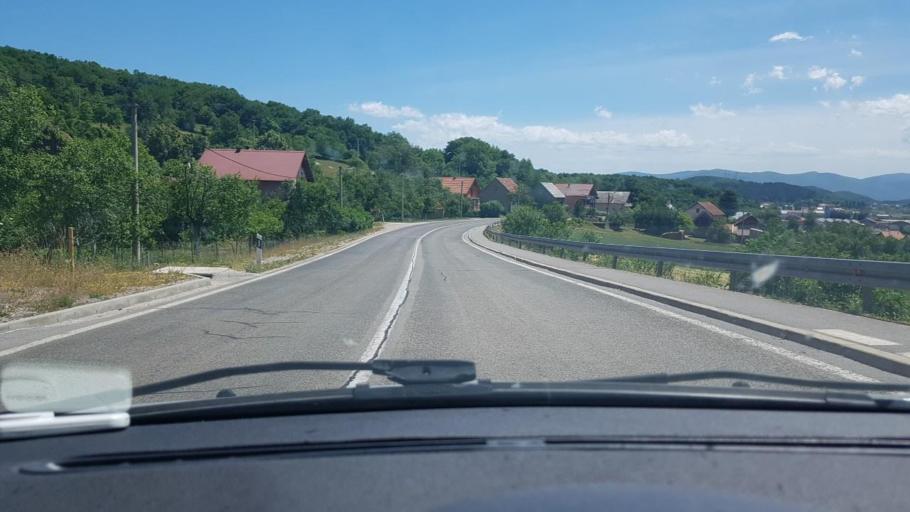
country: HR
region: Licko-Senjska
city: Otocac
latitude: 44.8741
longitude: 15.2102
